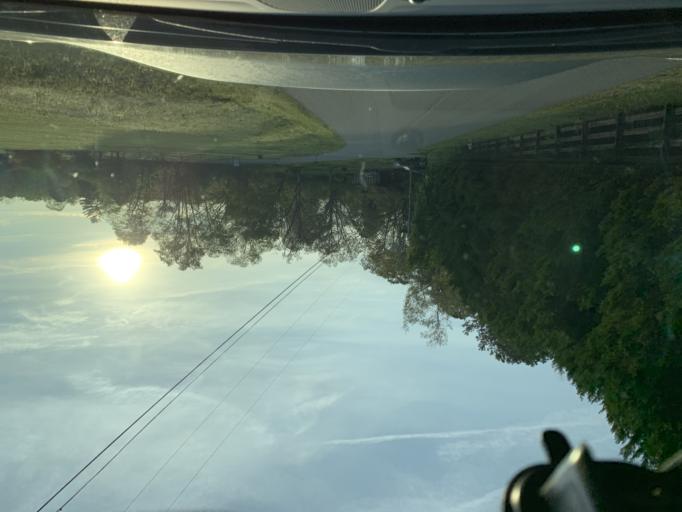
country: US
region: Georgia
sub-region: Forsyth County
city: Cumming
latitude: 34.2501
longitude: -84.1878
